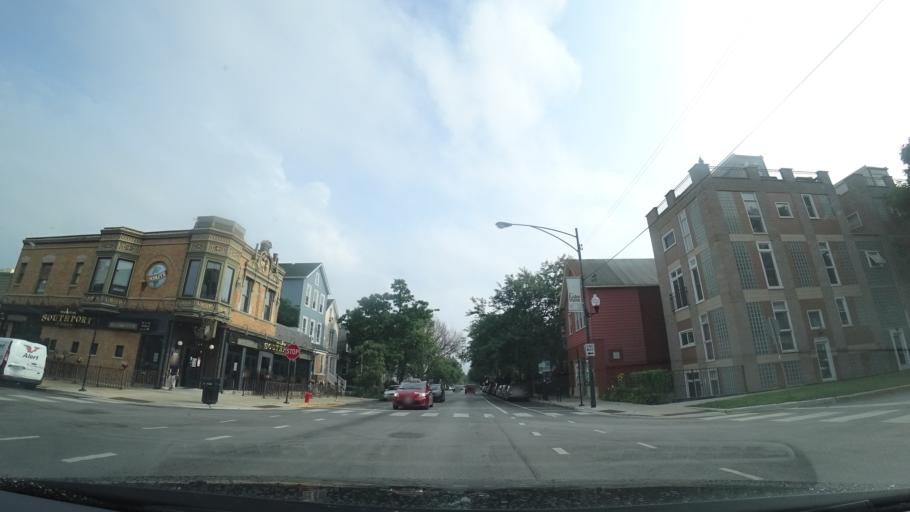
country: US
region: Illinois
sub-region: Cook County
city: Lincolnwood
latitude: 41.9426
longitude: -87.6639
